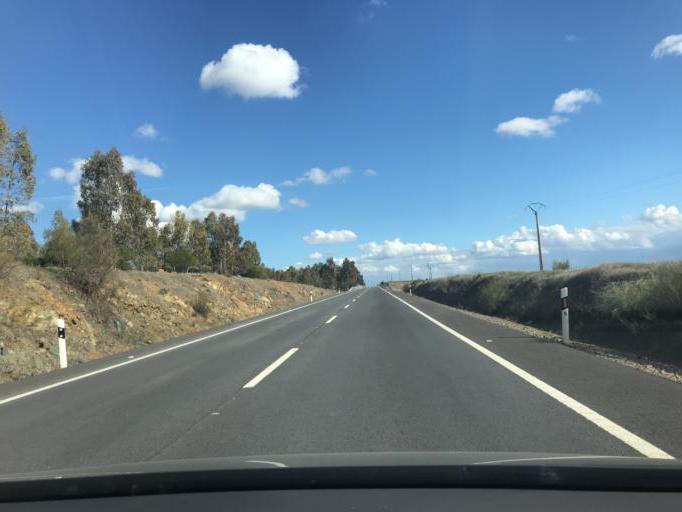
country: ES
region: Extremadura
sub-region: Provincia de Badajoz
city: Granja de Torrehermosa
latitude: 38.3012
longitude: -5.6035
